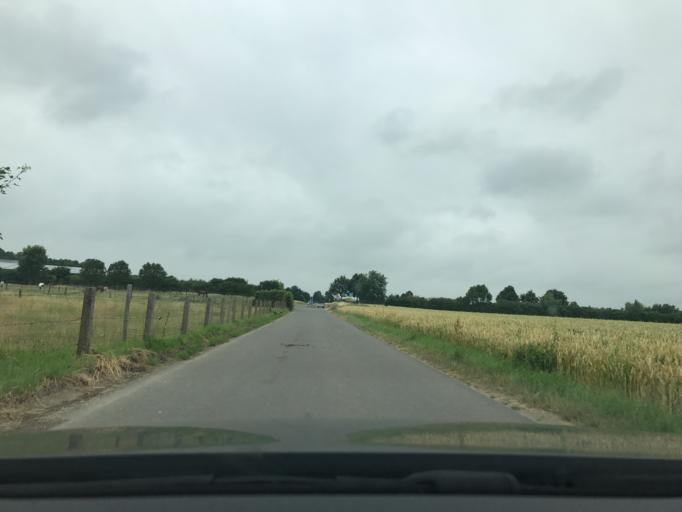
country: DE
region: North Rhine-Westphalia
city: Kempen
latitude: 51.3412
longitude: 6.3867
